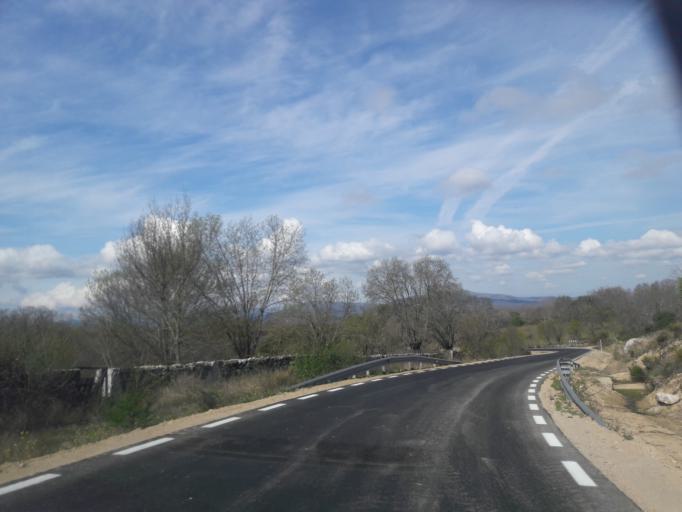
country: ES
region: Castille and Leon
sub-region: Provincia de Salamanca
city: Endrinal
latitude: 40.5382
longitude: -5.8083
